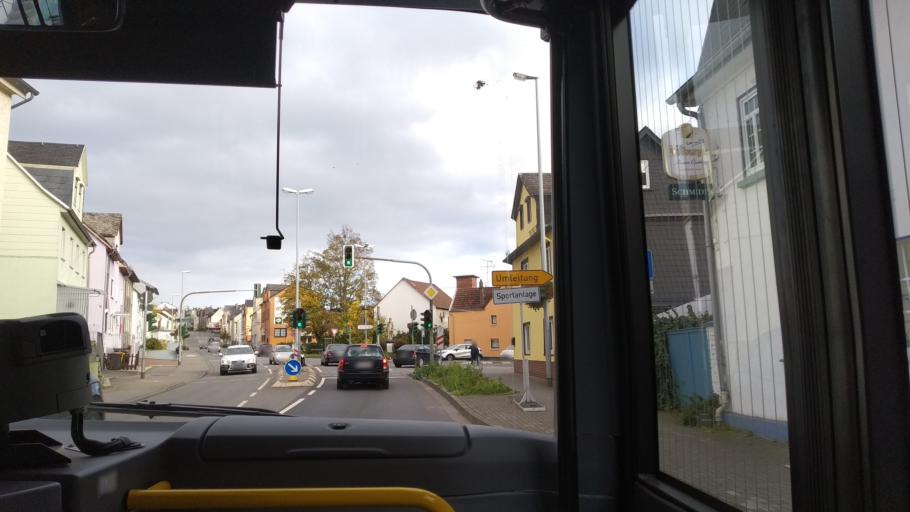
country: DE
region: Rheinland-Pfalz
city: Diez
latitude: 50.3700
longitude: 8.0233
